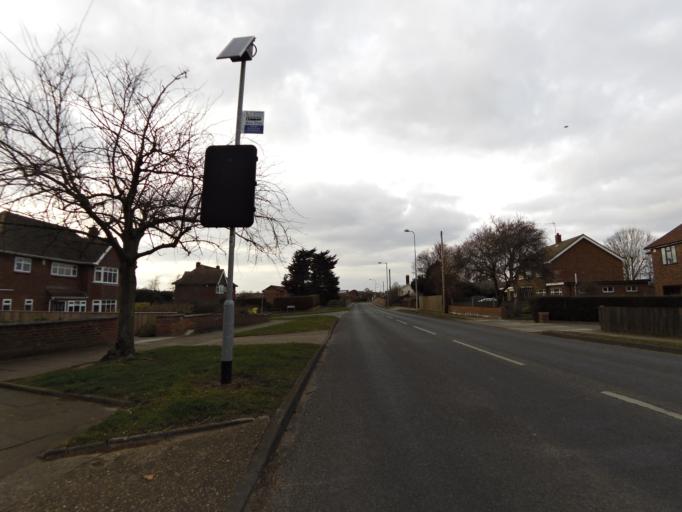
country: GB
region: England
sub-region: Suffolk
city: Ipswich
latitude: 52.0776
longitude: 1.1515
